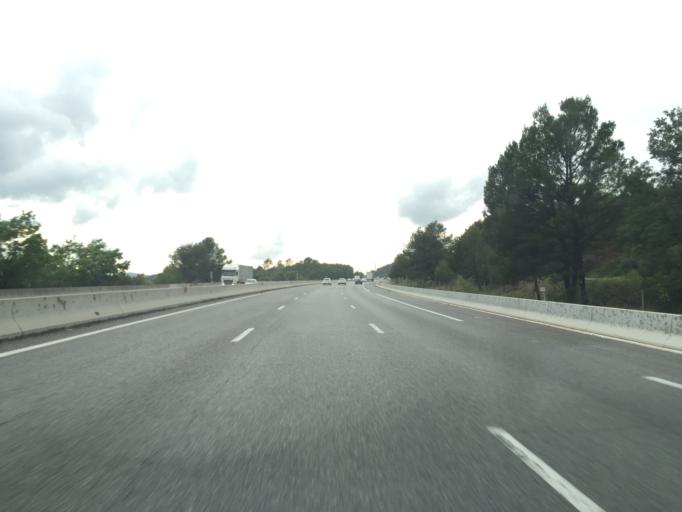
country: FR
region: Provence-Alpes-Cote d'Azur
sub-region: Departement du Var
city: Cabasse
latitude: 43.4090
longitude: 6.1630
